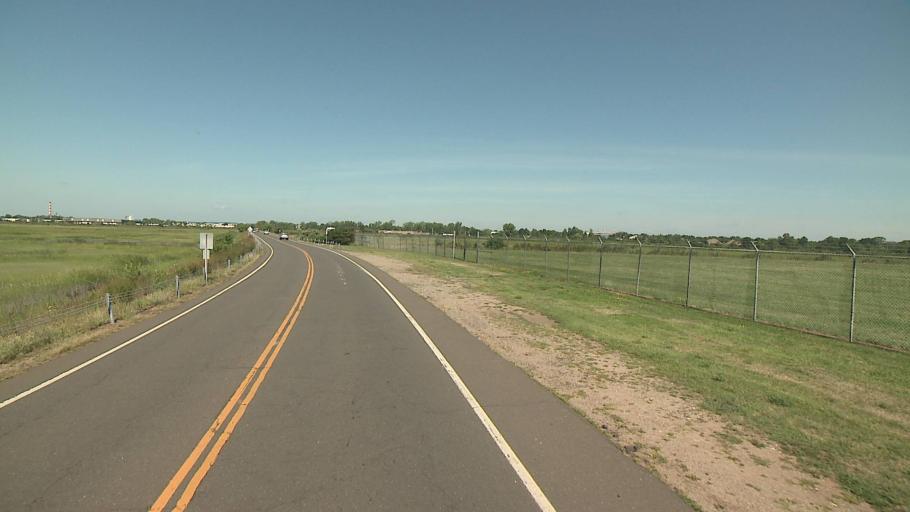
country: US
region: Connecticut
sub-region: Fairfield County
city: Stratford
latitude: 41.1624
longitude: -73.1344
